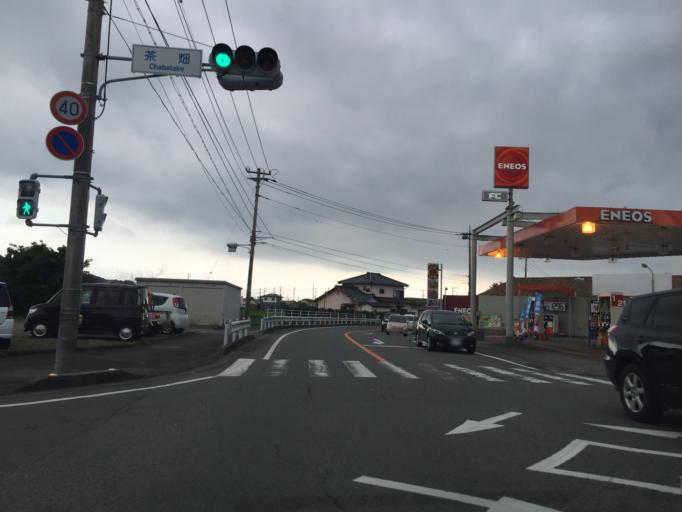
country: JP
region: Shizuoka
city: Mishima
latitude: 35.1705
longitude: 138.9197
